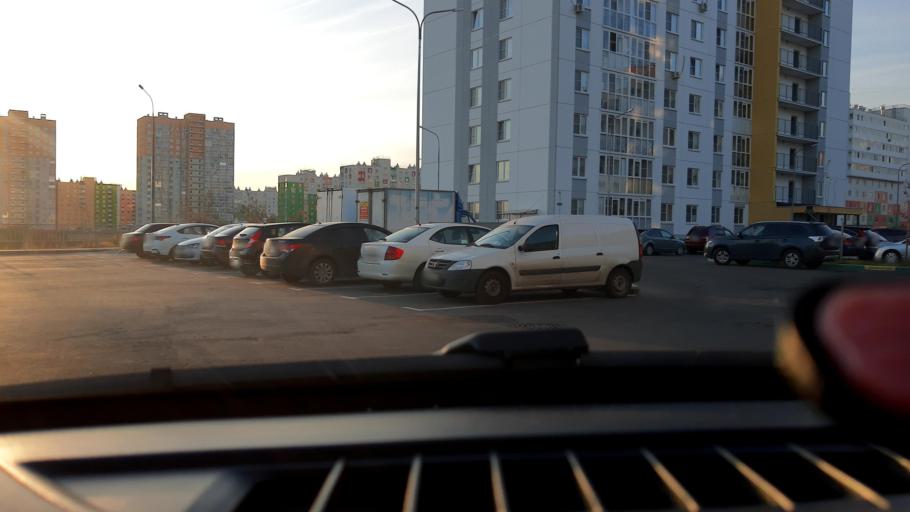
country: RU
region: Nizjnij Novgorod
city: Nizhniy Novgorod
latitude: 56.3450
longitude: 43.9080
